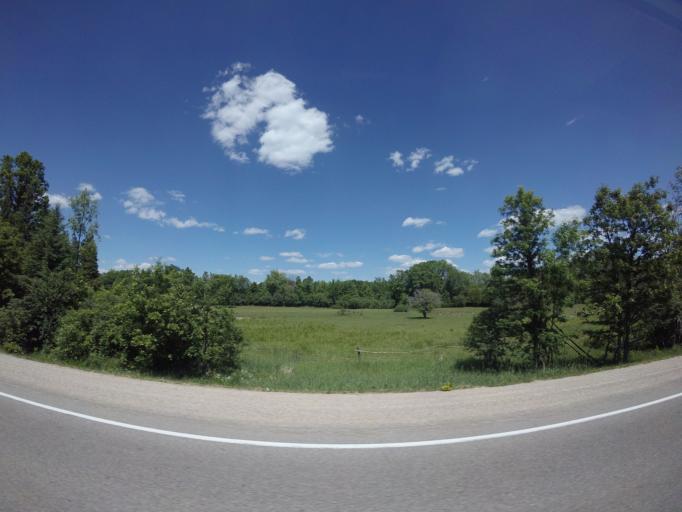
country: CA
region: Ontario
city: Perth
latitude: 45.0190
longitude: -76.2349
